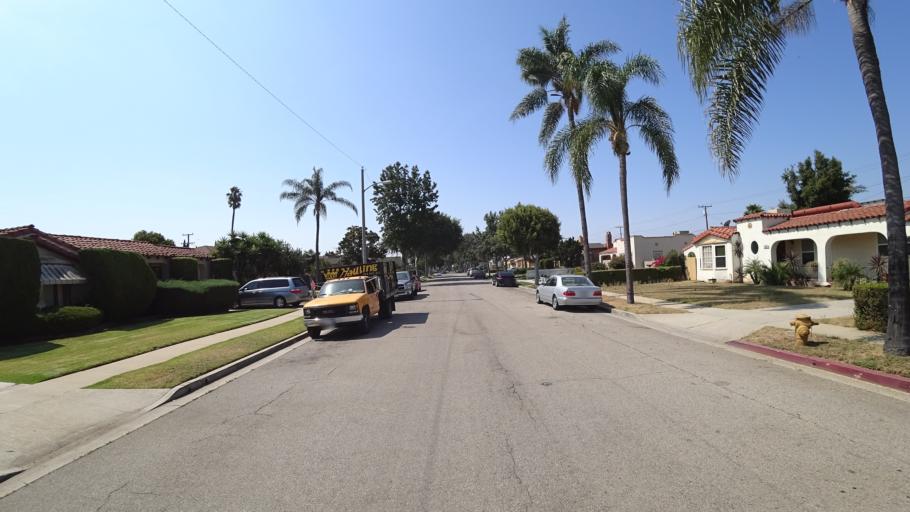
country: US
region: California
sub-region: Los Angeles County
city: Westmont
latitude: 33.9540
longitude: -118.3188
